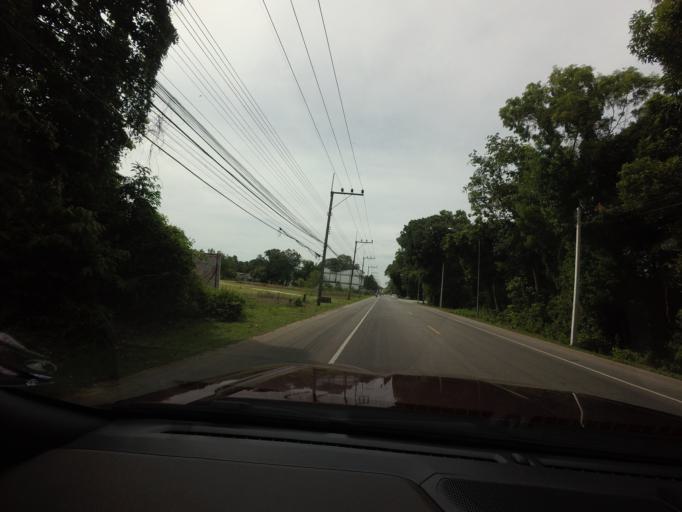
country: TH
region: Narathiwat
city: Tak Bai
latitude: 6.2441
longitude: 102.0747
